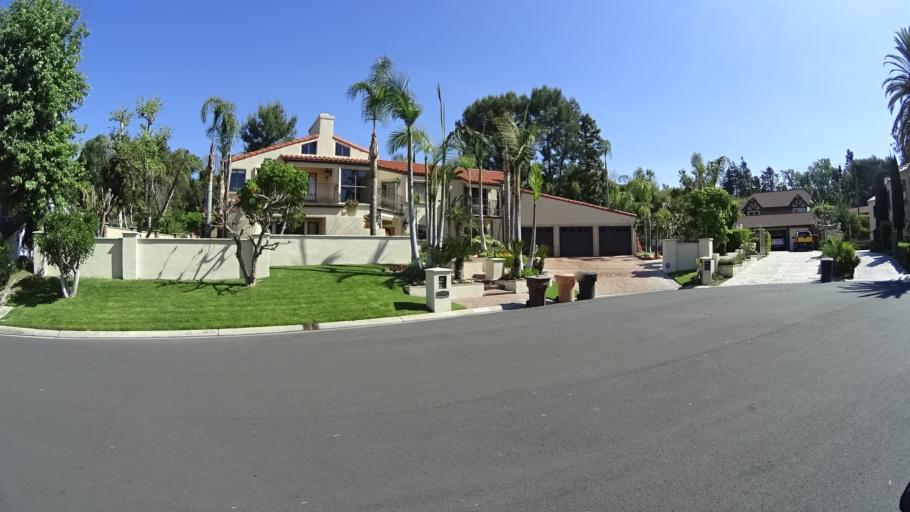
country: US
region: California
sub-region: Orange County
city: Villa Park
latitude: 33.8197
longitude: -117.8019
